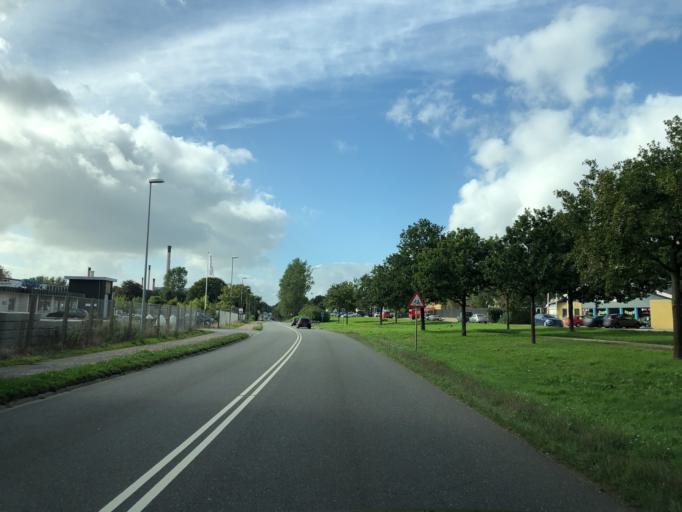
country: DK
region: Central Jutland
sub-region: Holstebro Kommune
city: Holstebro
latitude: 56.3647
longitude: 8.5901
